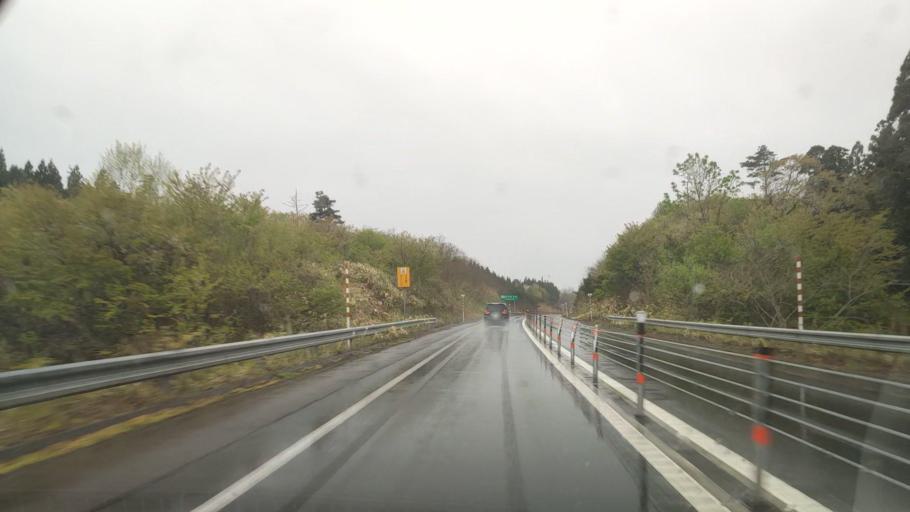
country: JP
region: Akita
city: Noshiromachi
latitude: 40.1642
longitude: 140.0460
